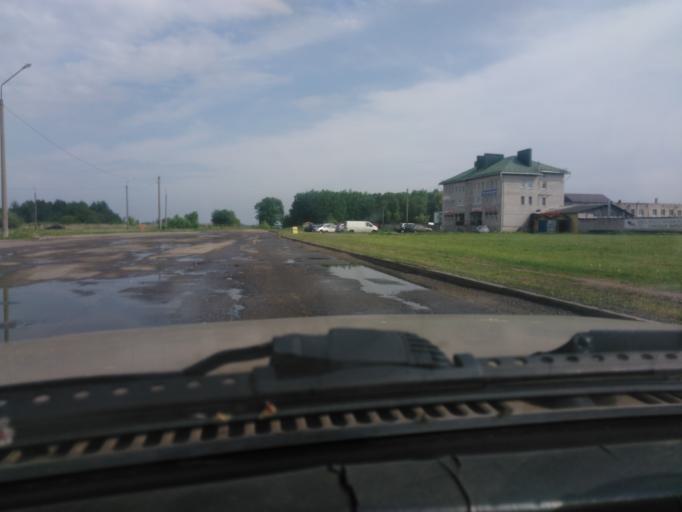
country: BY
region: Mogilev
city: Mahilyow
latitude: 53.9441
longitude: 30.3658
